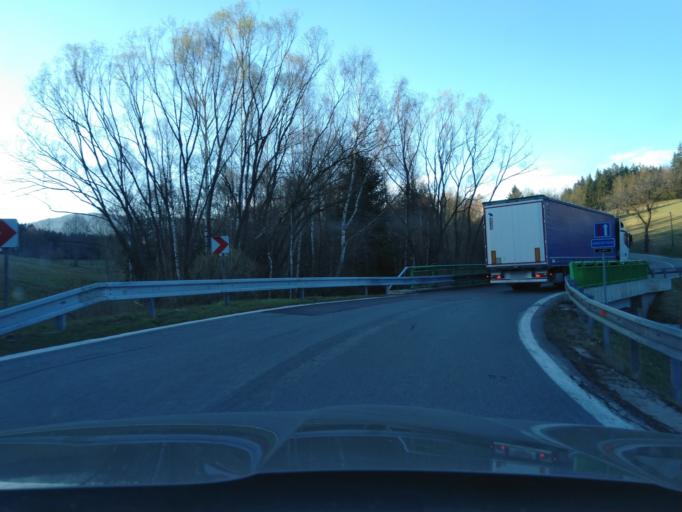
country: CZ
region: Jihocesky
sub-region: Okres Prachatice
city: Vimperk
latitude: 49.0254
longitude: 13.7667
